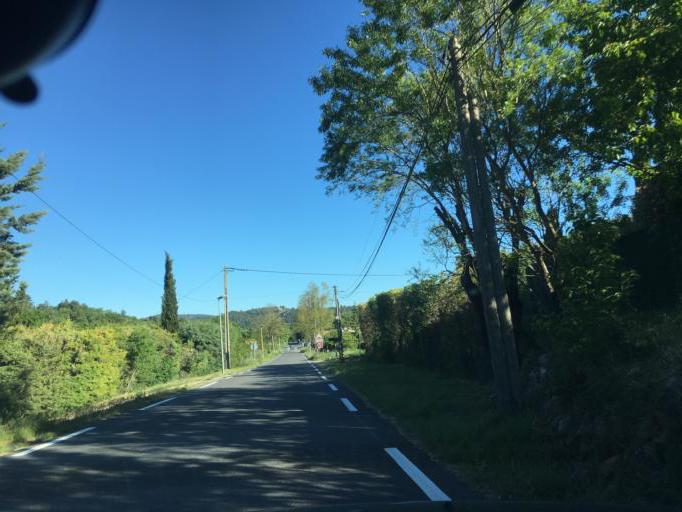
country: FR
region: Provence-Alpes-Cote d'Azur
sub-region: Departement du Var
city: Rians
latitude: 43.6058
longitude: 5.7661
